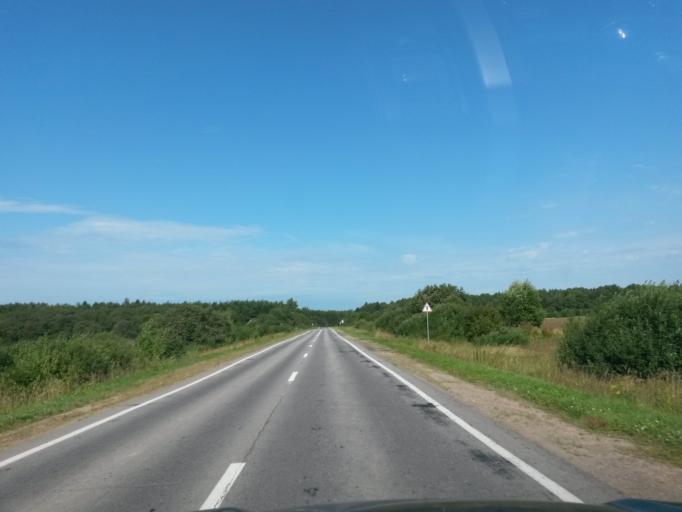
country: RU
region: Jaroslavl
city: Konstantinovskiy
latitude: 57.8504
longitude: 39.6288
